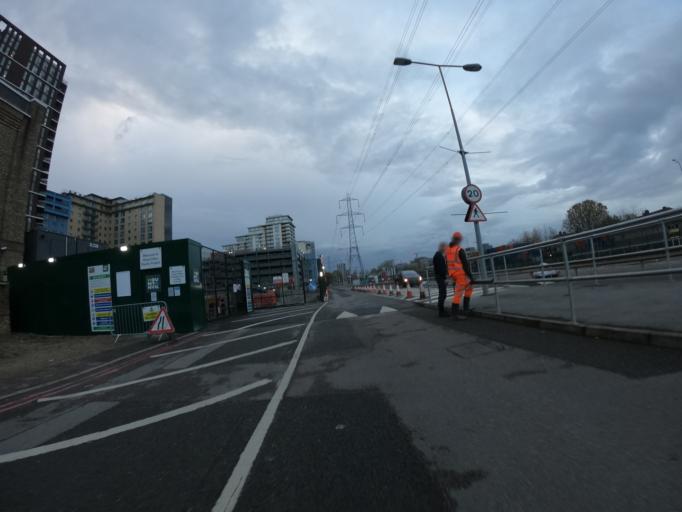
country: GB
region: England
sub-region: Greater London
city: East Ham
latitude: 51.5092
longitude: 0.0227
